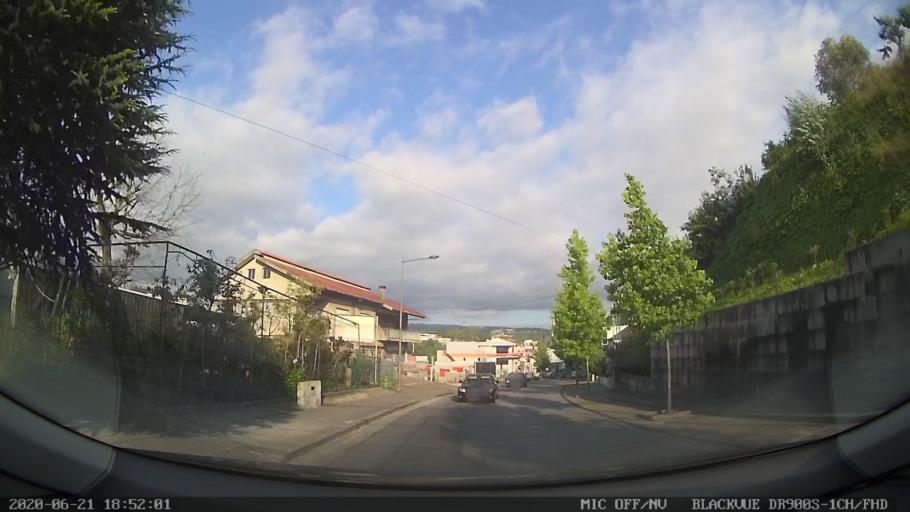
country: PT
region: Porto
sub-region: Amarante
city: Amarante
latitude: 41.2804
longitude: -8.0838
